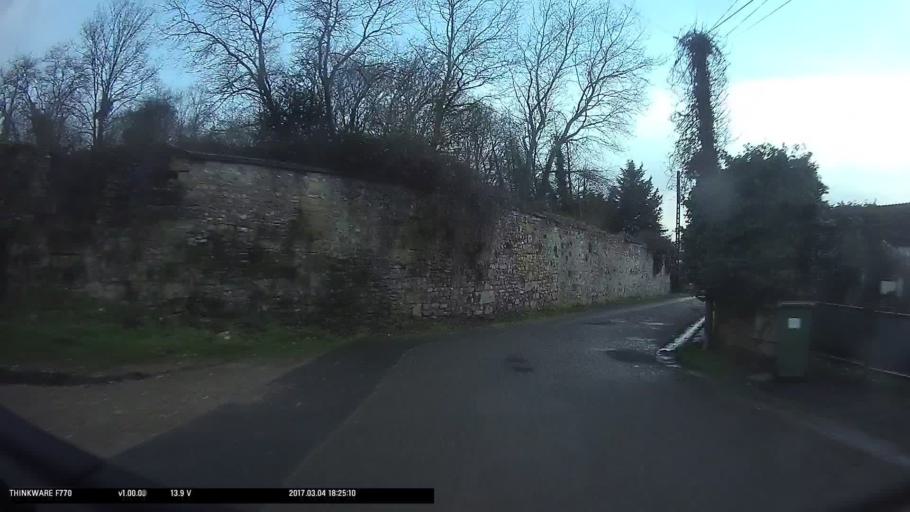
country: FR
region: Ile-de-France
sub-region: Departement du Val-d'Oise
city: Ableiges
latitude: 49.1165
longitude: 2.0155
